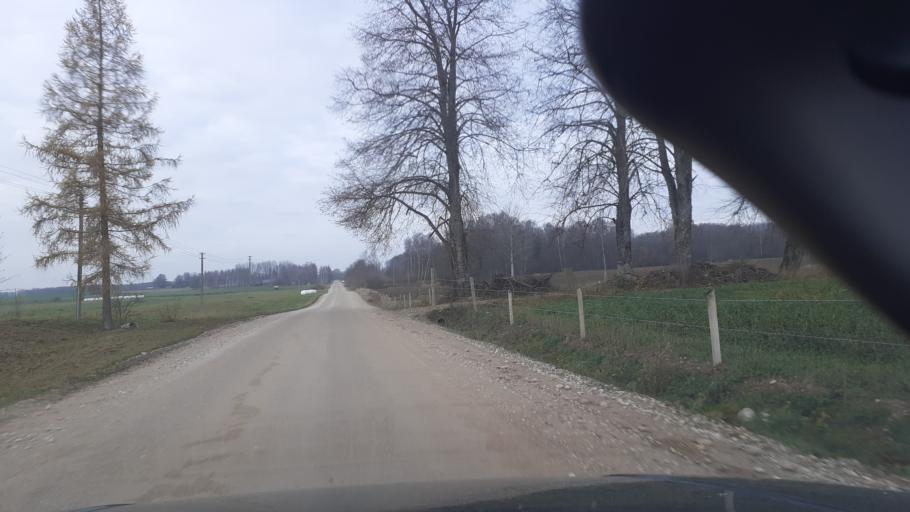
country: LV
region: Alsunga
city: Alsunga
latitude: 56.9132
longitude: 21.6560
